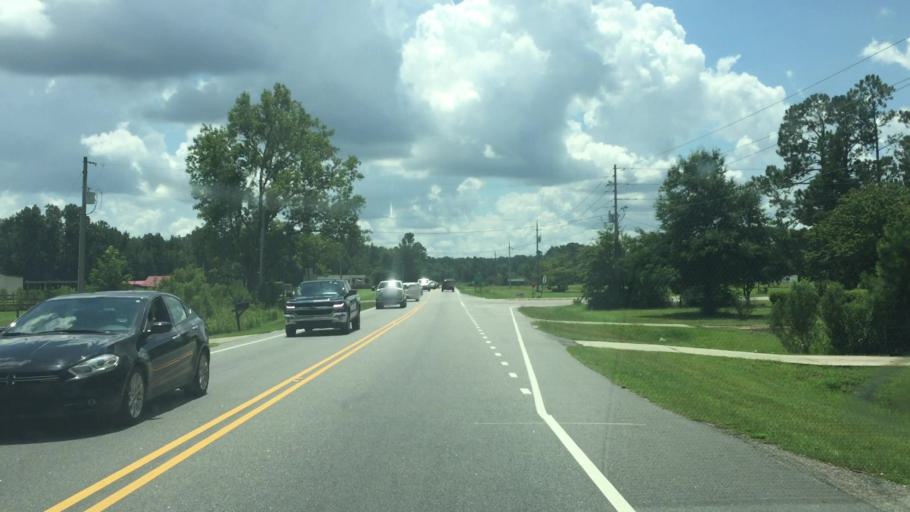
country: US
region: North Carolina
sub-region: Columbus County
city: Chadbourn
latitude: 34.3566
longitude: -78.8297
